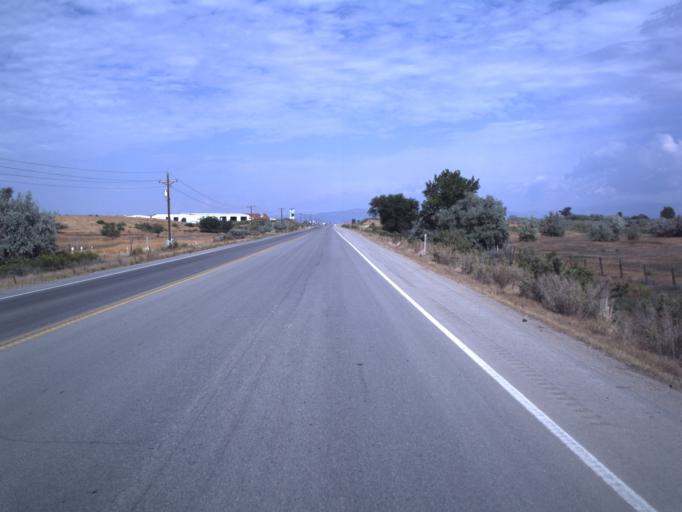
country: US
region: Utah
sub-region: Uintah County
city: Naples
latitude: 40.3849
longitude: -109.4307
